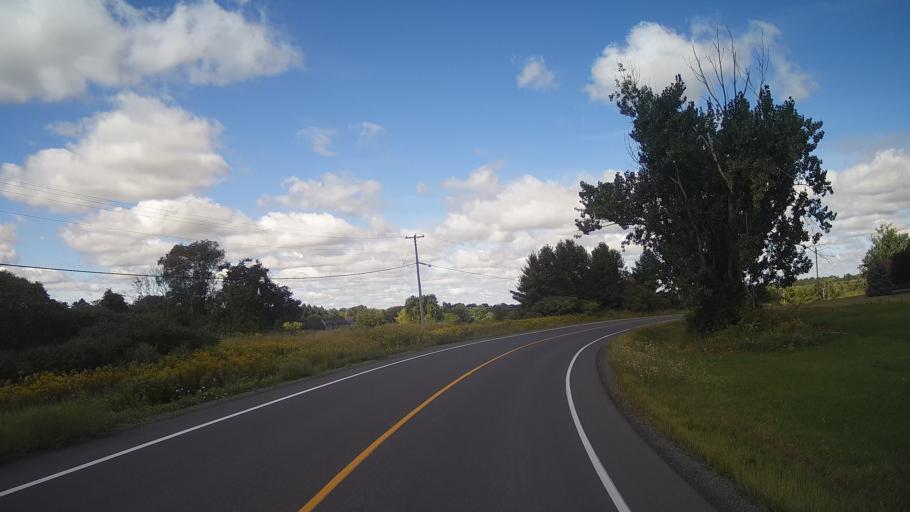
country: US
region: New York
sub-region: St. Lawrence County
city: Ogdensburg
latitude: 44.8584
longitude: -75.2728
